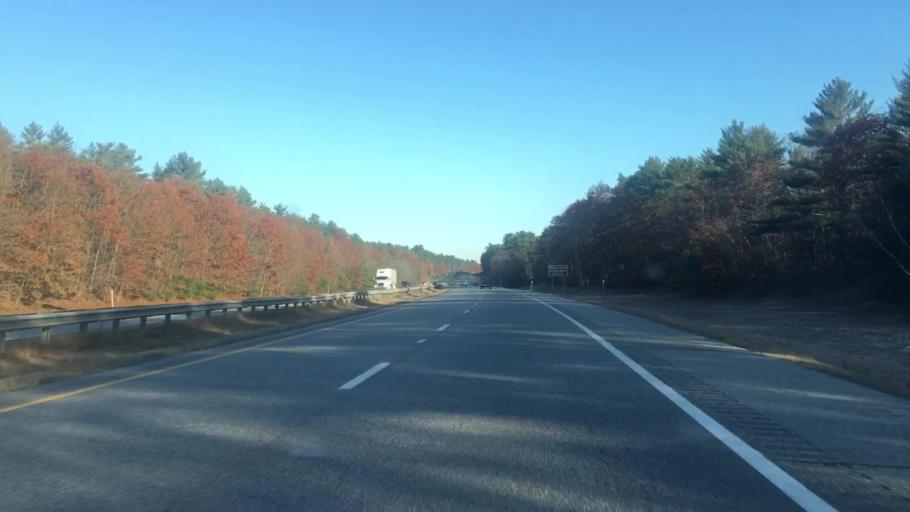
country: US
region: Maine
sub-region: Cumberland County
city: New Gloucester
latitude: 43.9860
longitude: -70.3097
